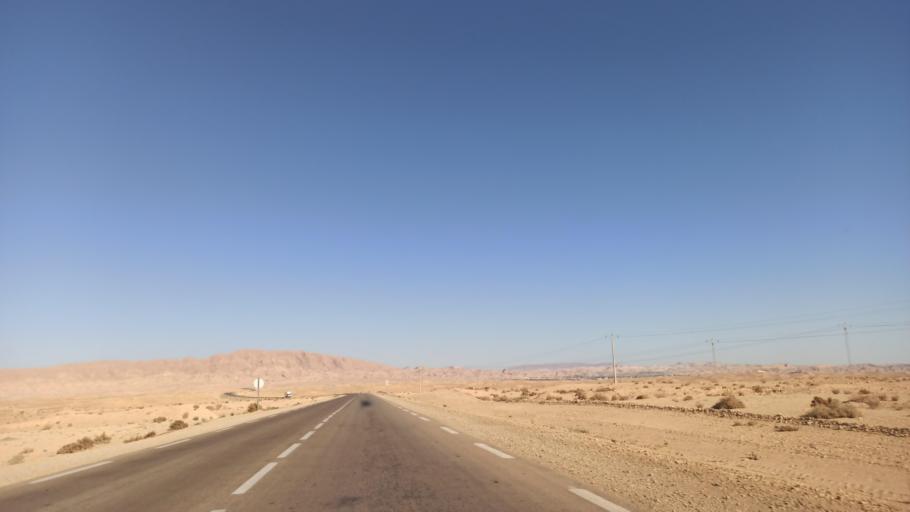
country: TN
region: Gafsa
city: Al Metlaoui
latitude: 34.2796
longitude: 8.3517
